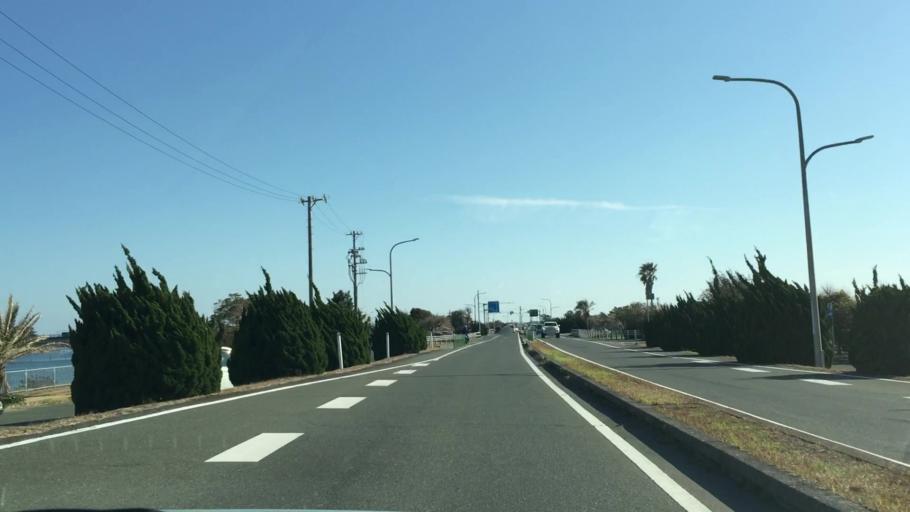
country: JP
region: Shizuoka
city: Kosai-shi
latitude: 34.7062
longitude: 137.6102
